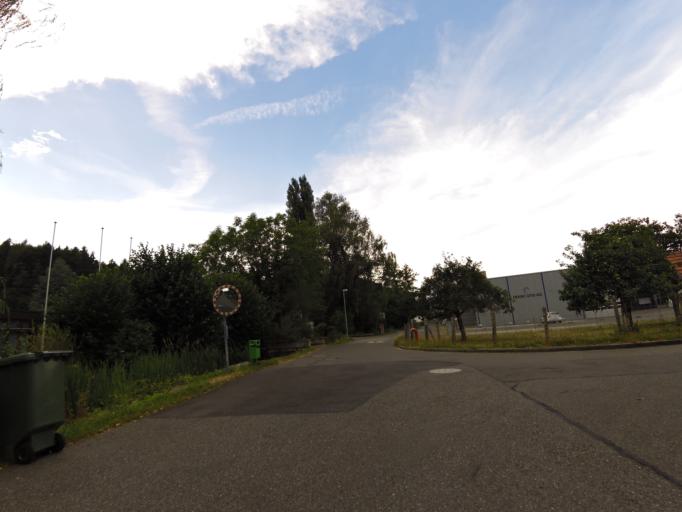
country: CH
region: Aargau
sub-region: Bezirk Aarau
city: Suhr
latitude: 47.3779
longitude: 8.0748
